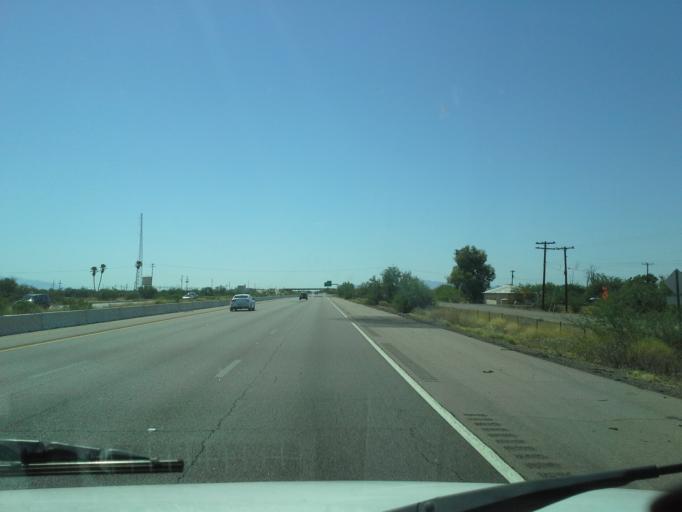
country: US
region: Arizona
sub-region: Pima County
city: Avra Valley
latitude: 32.5803
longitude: -111.3293
